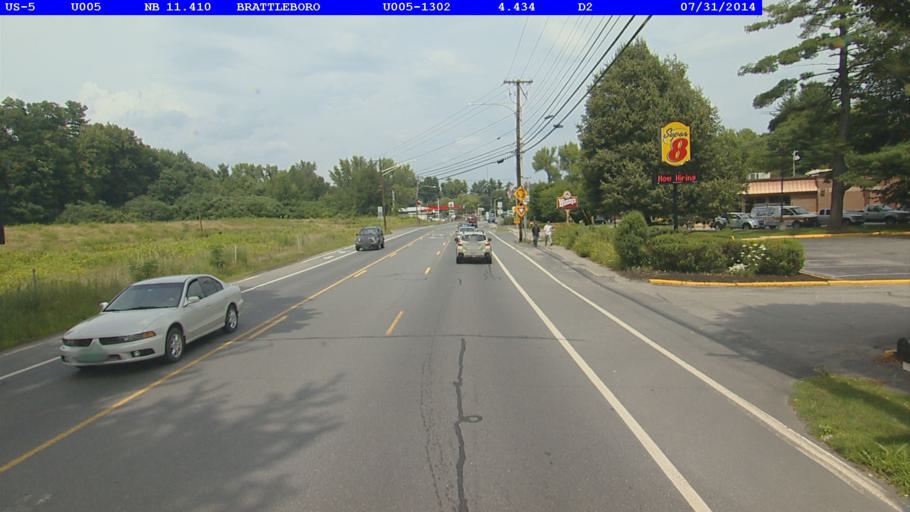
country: US
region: Vermont
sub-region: Windham County
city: Brattleboro
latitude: 42.8825
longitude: -72.5581
